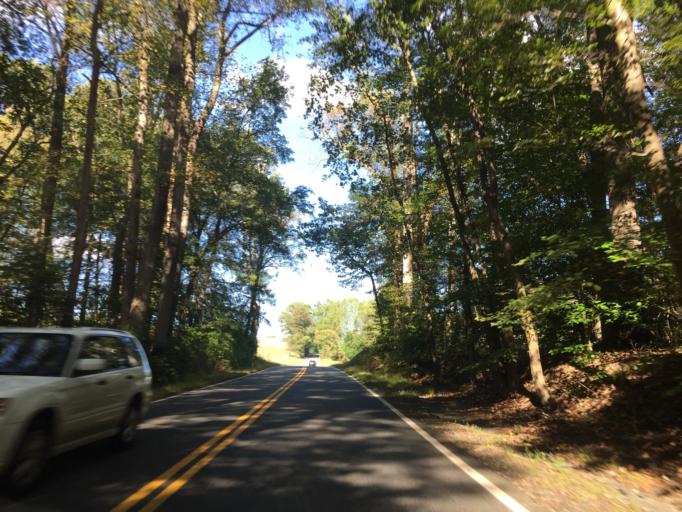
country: US
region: Maryland
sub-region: Harford County
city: Fallston
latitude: 39.5106
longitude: -76.4589
